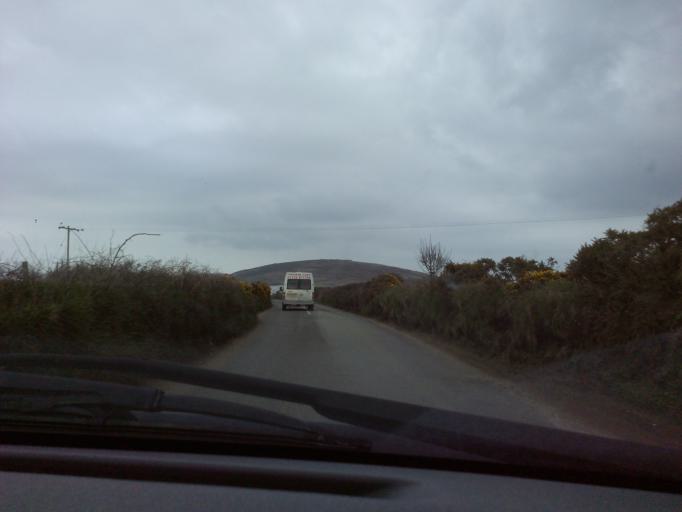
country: GB
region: England
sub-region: Cornwall
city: Sennen
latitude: 50.0879
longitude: -5.6696
